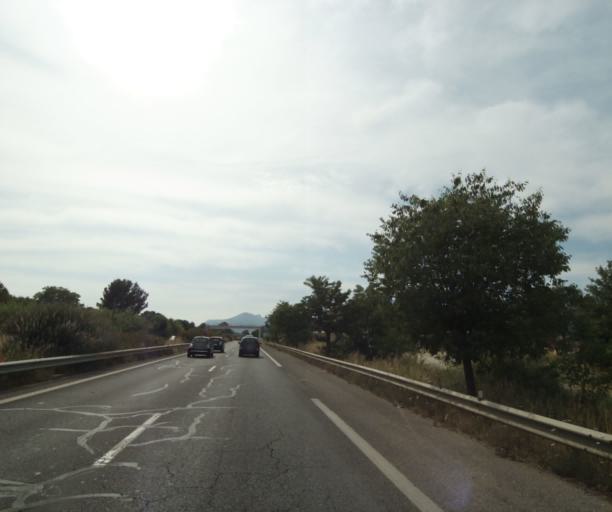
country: FR
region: Provence-Alpes-Cote d'Azur
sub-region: Departement du Var
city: La Crau
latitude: 43.1321
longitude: 6.0626
